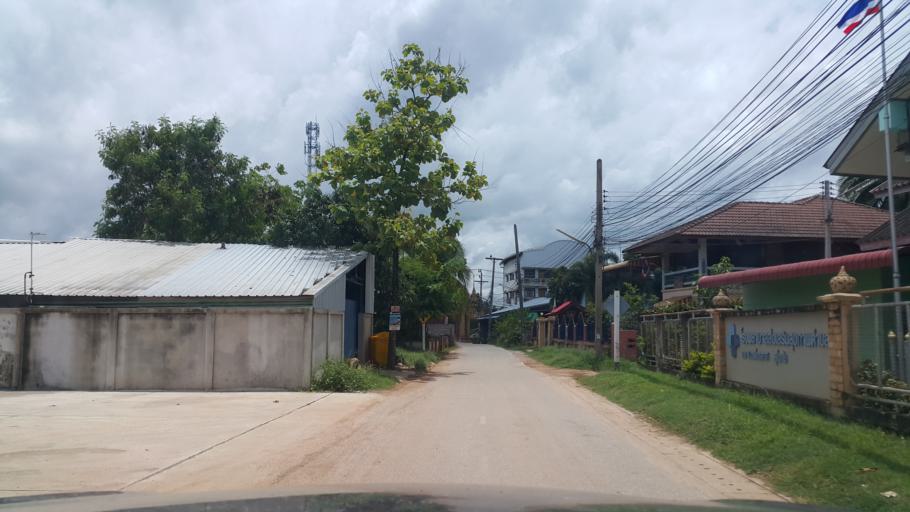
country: TH
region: Sukhothai
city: Kong Krailat
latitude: 16.9318
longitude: 99.9585
